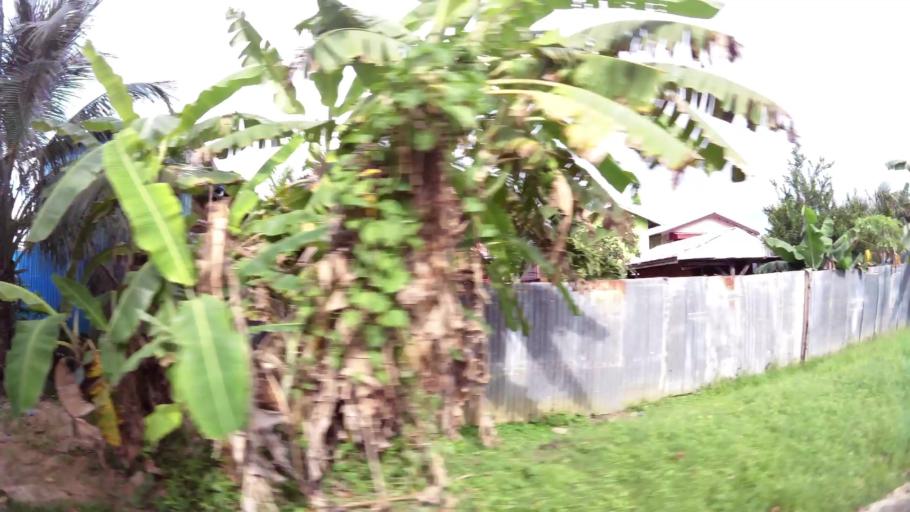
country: SR
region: Paramaribo
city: Paramaribo
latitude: 5.8514
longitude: -55.1552
